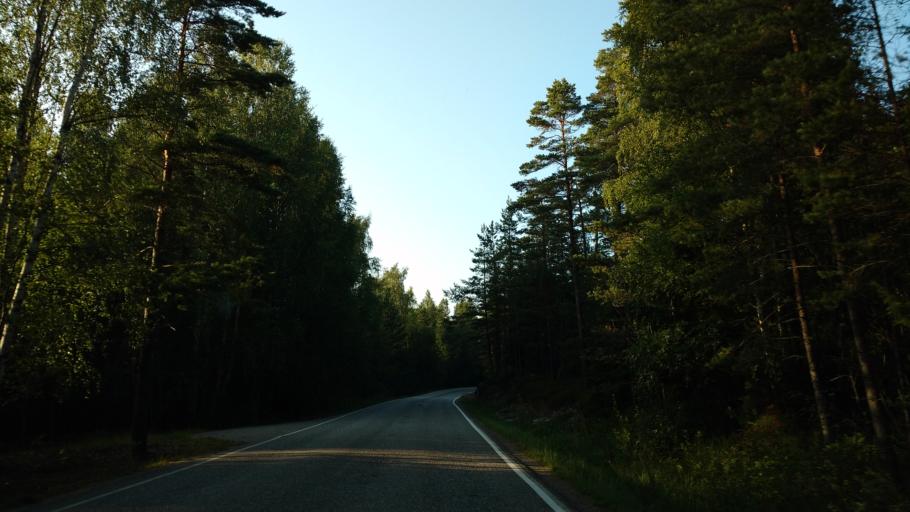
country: FI
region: Varsinais-Suomi
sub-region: Aboland-Turunmaa
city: Dragsfjaerd
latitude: 60.0246
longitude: 22.4593
